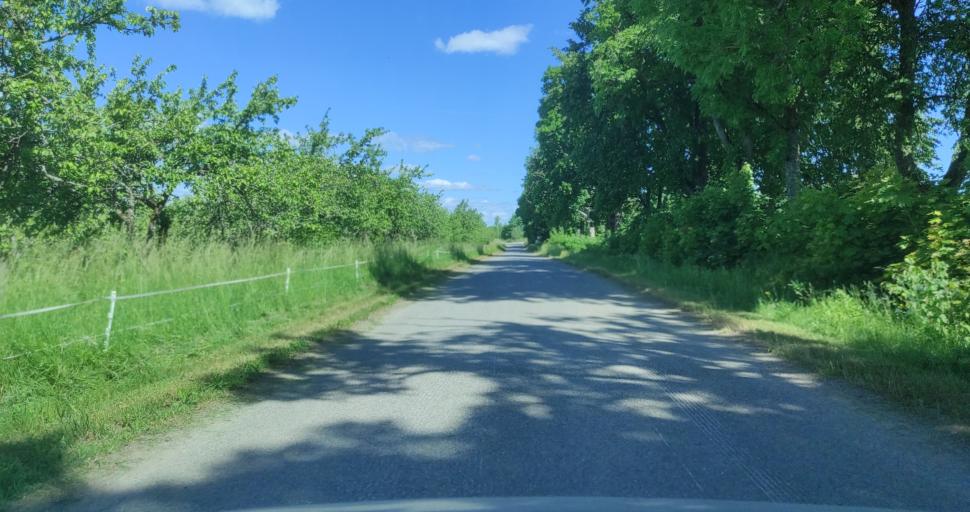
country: LV
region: Kuldigas Rajons
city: Kuldiga
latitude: 56.9388
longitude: 21.8246
